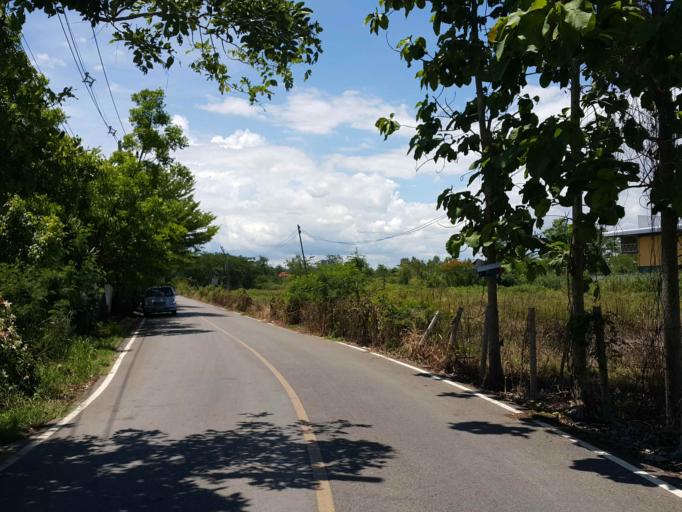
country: TH
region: Chiang Mai
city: Saraphi
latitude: 18.7457
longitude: 99.0007
